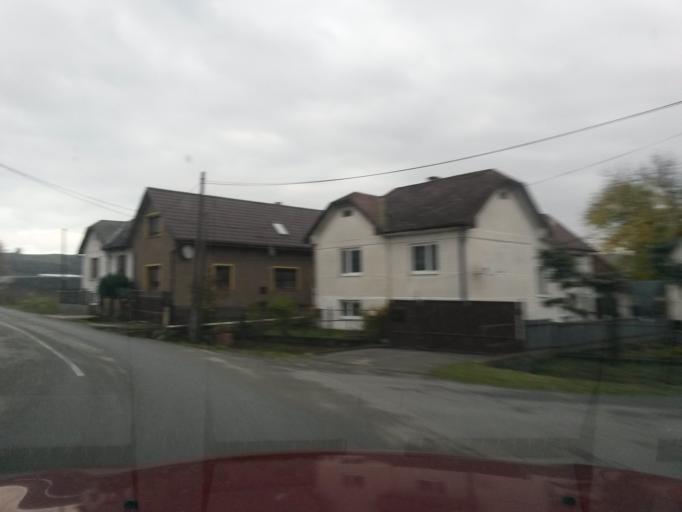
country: SK
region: Kosicky
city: Kosice
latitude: 48.8037
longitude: 21.2502
